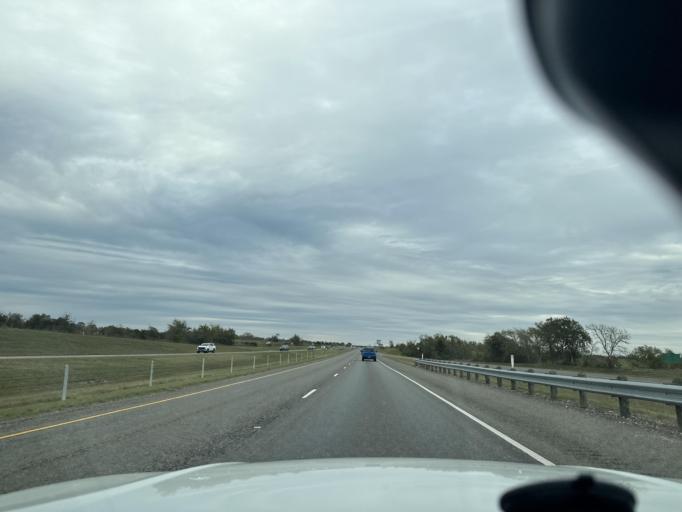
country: US
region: Texas
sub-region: Burleson County
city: Somerville
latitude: 30.1529
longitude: -96.6271
